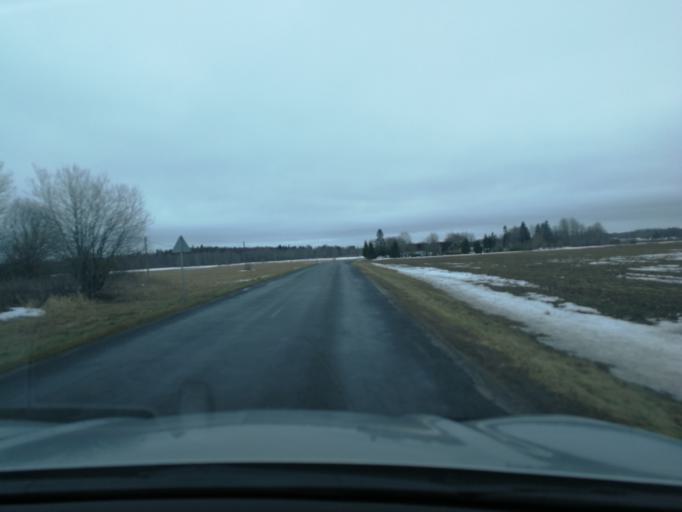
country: EE
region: Harju
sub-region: Kiili vald
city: Kiili
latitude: 59.2895
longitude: 24.8753
